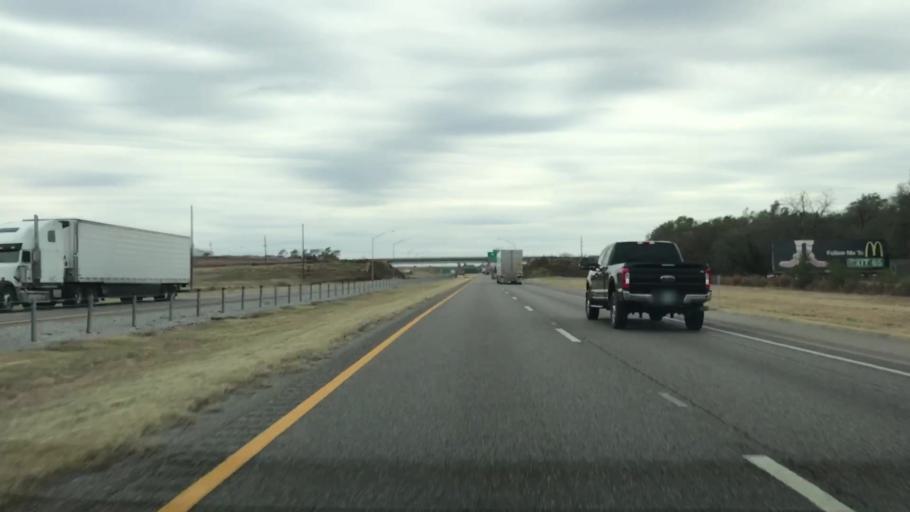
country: US
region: Oklahoma
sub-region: Custer County
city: Clinton
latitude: 35.5002
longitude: -98.9556
